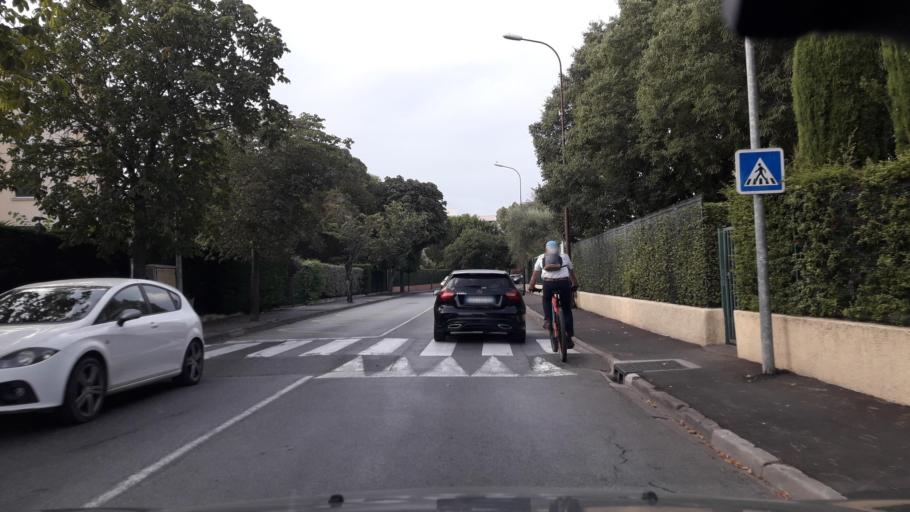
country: FR
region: Provence-Alpes-Cote d'Azur
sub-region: Departement du Var
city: Frejus
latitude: 43.4360
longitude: 6.7541
